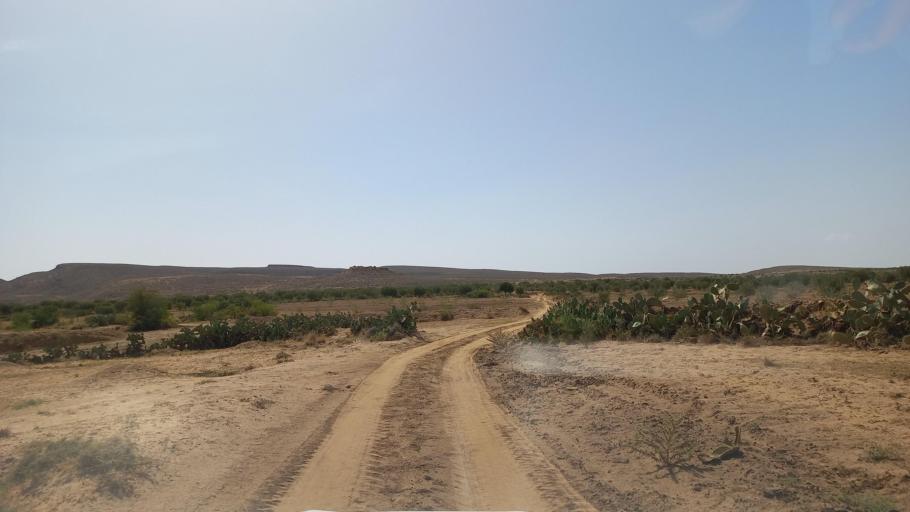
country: TN
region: Al Qasrayn
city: Kasserine
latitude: 35.1991
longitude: 9.0296
